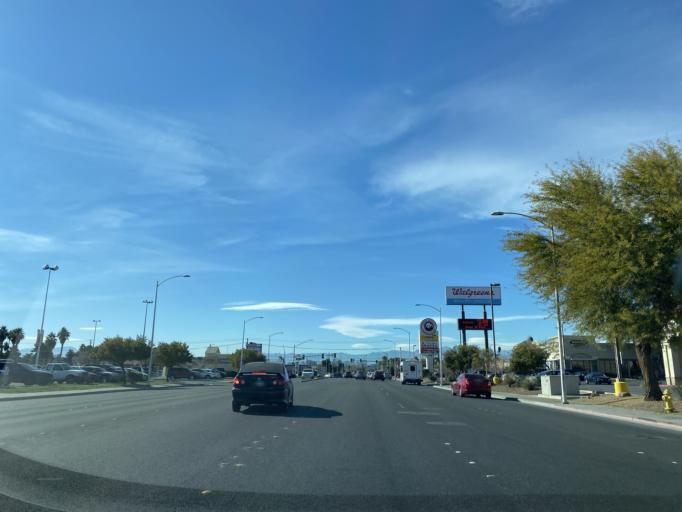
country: US
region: Nevada
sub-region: Clark County
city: Sunrise Manor
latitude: 36.1736
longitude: -115.0784
